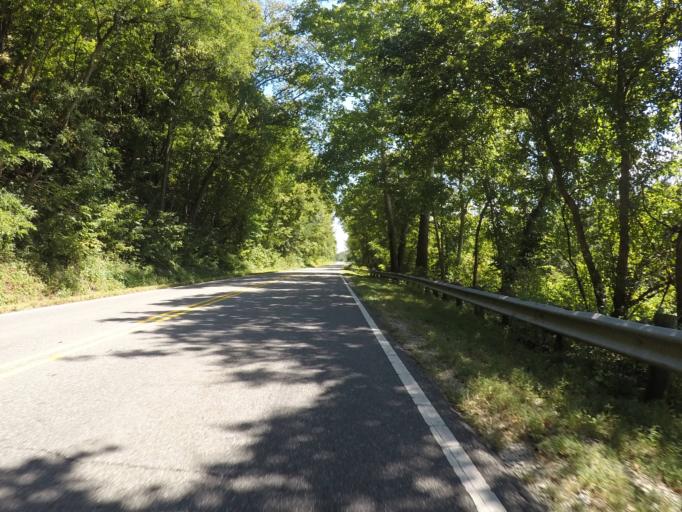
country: US
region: West Virginia
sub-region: Wayne County
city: Ceredo
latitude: 38.4059
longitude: -82.5637
